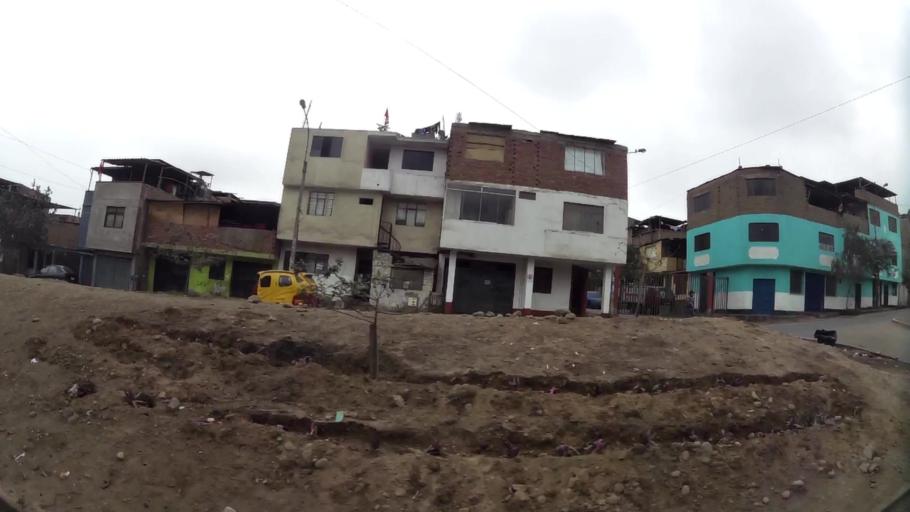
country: PE
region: Lima
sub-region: Lima
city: Surco
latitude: -12.1350
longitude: -76.9585
